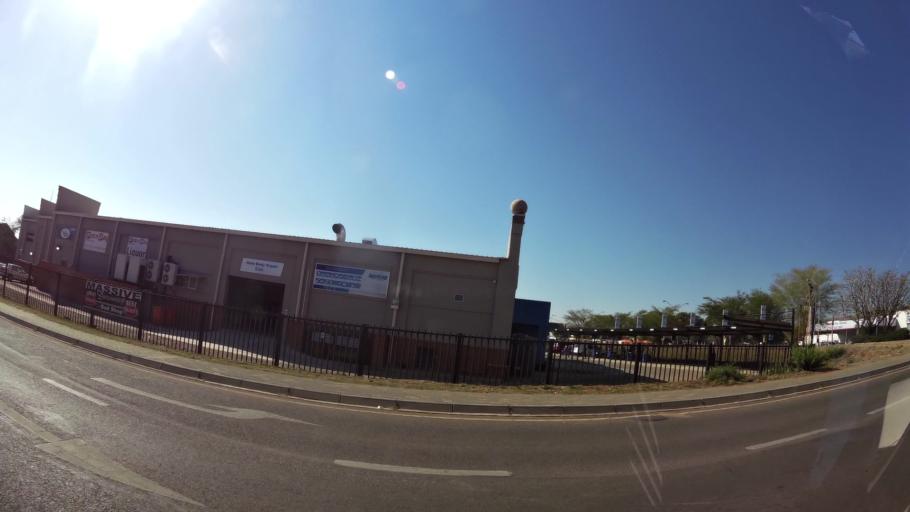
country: ZA
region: Gauteng
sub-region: City of Tshwane Metropolitan Municipality
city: Pretoria
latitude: -25.6787
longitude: 28.2375
